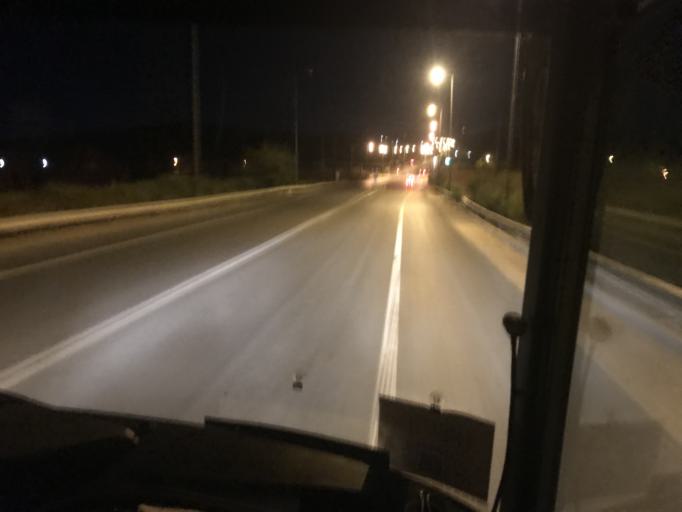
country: GR
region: Crete
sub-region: Nomos Irakleiou
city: Skalanion
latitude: 35.2804
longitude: 25.1804
